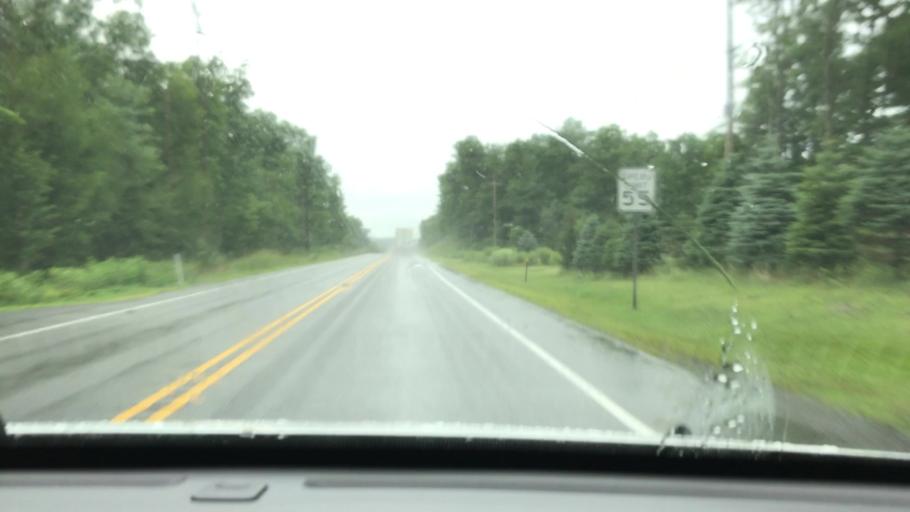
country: US
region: Pennsylvania
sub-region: Clearfield County
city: Osceola Mills
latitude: 40.8125
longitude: -78.2249
